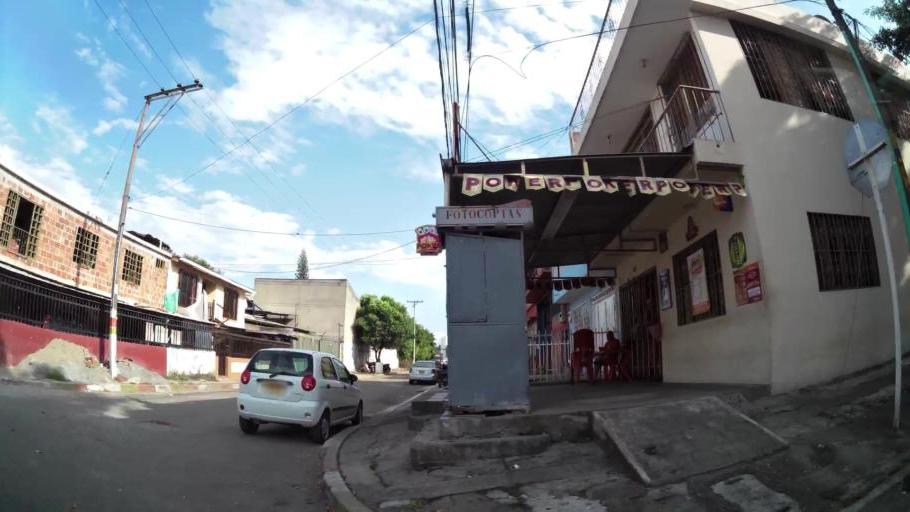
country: CO
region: Valle del Cauca
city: Cali
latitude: 3.4695
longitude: -76.5135
